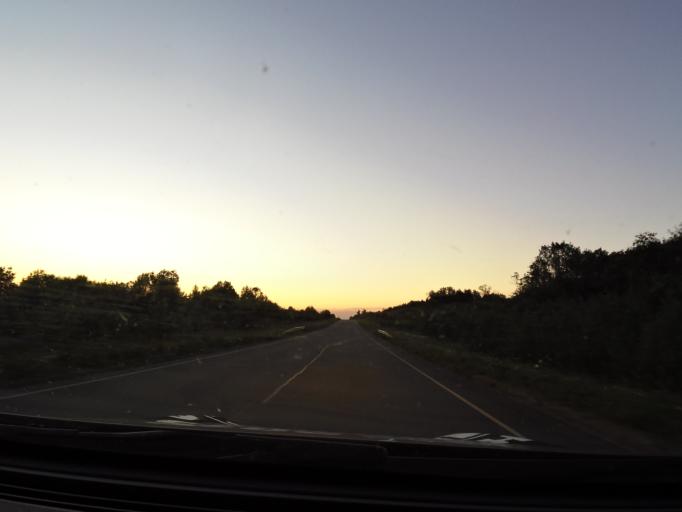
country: RU
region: Vologda
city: Vytegra
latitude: 60.9450
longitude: 36.0909
